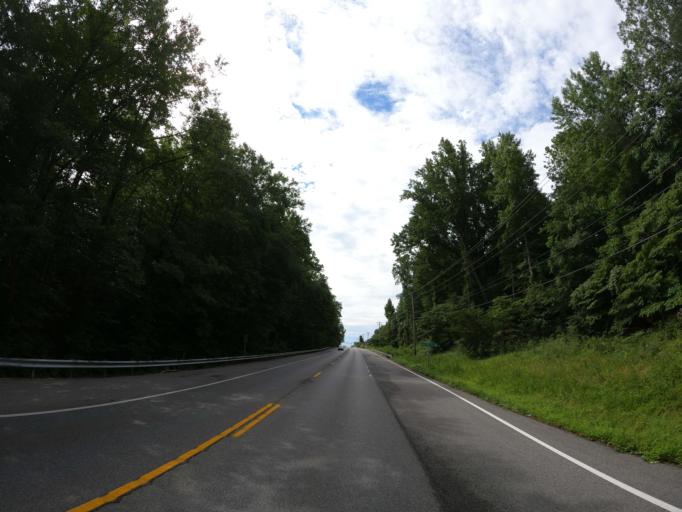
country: US
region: Maryland
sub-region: Saint Mary's County
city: Leonardtown
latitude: 38.2794
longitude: -76.6137
